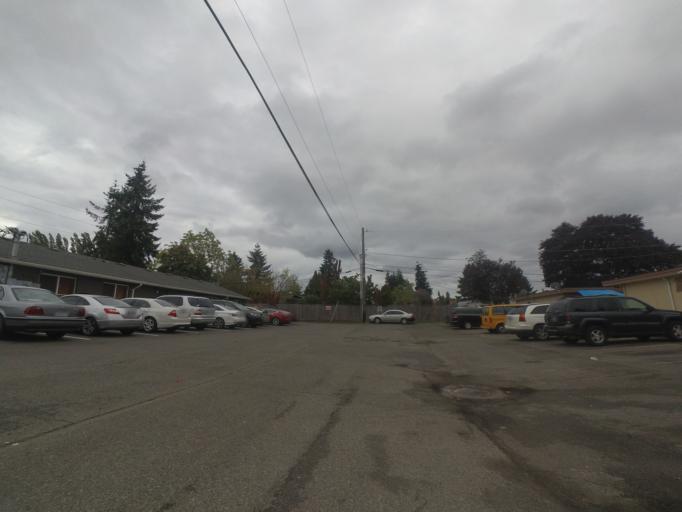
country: US
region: Washington
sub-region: Pierce County
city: Lakewood
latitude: 47.1543
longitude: -122.5054
